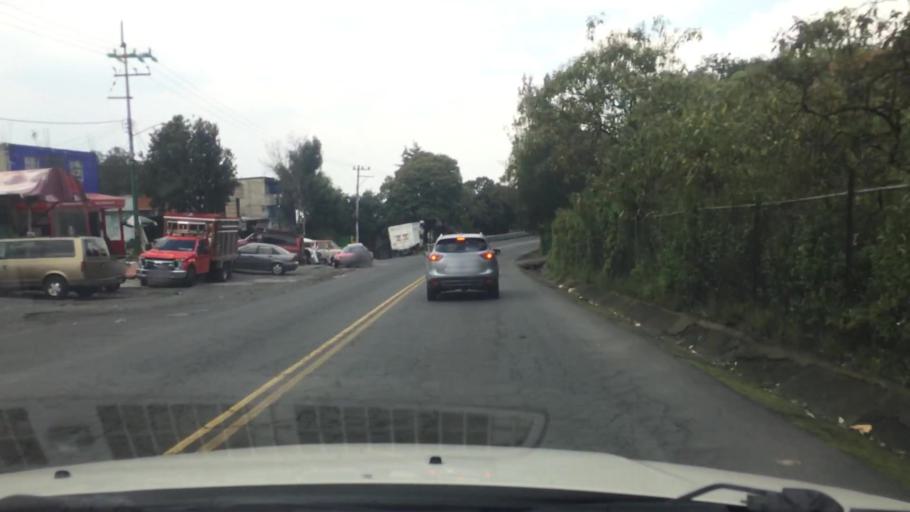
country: MX
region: Mexico City
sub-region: Tlalpan
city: Lomas de Tepemecatl
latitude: 19.2690
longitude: -99.2165
